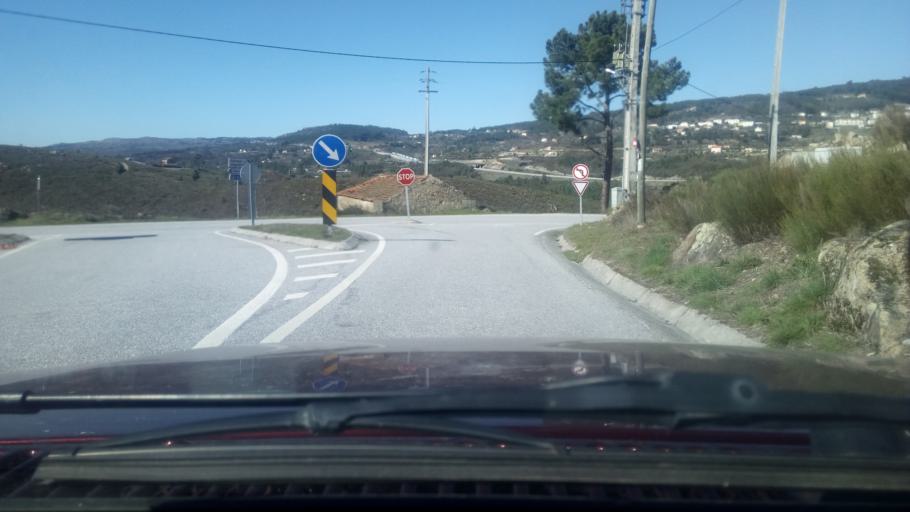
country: PT
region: Guarda
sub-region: Fornos de Algodres
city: Fornos de Algodres
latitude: 40.6041
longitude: -7.5252
